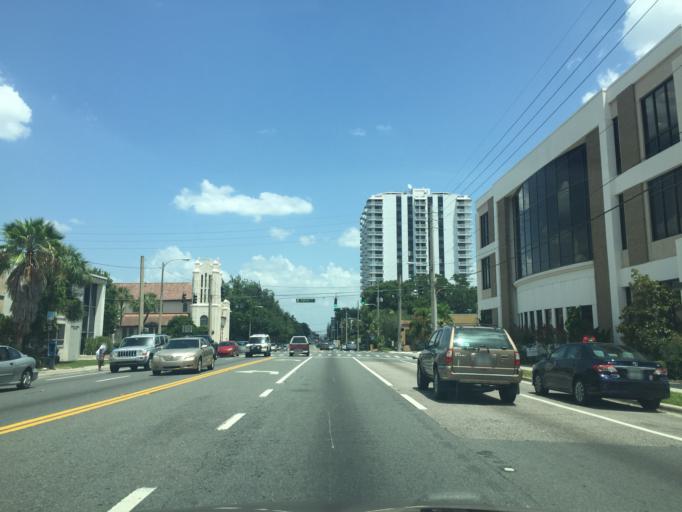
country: US
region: Florida
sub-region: Orange County
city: Orlando
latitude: 28.5531
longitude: -81.3745
